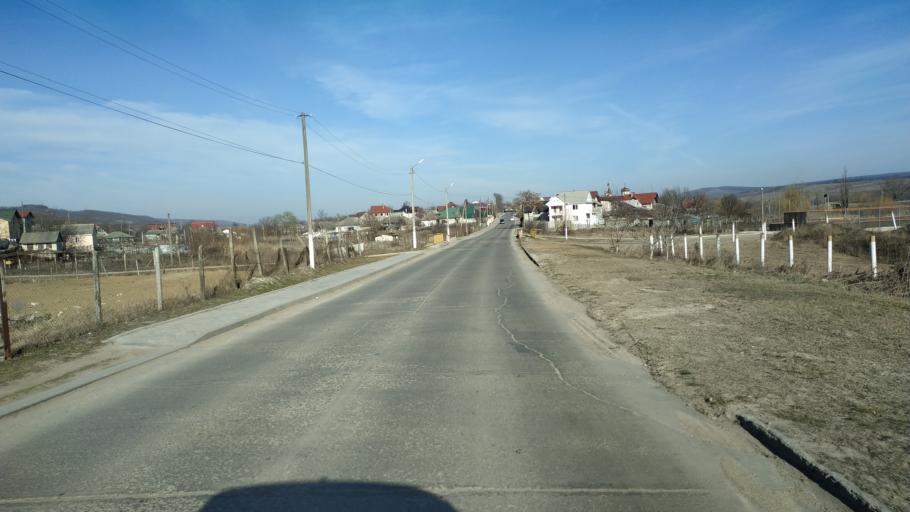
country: MD
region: Chisinau
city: Vatra
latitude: 47.0058
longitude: 28.6686
